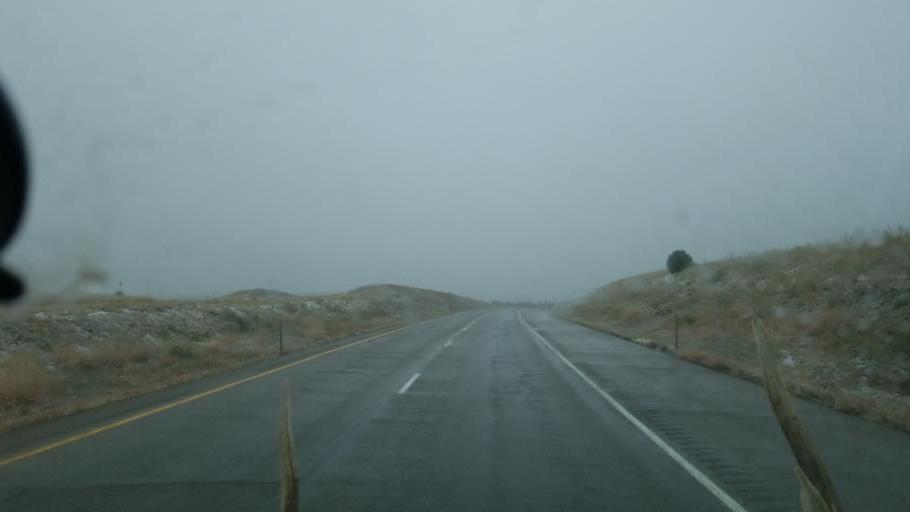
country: US
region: Colorado
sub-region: Pueblo County
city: Colorado City
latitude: 38.0393
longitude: -104.7290
